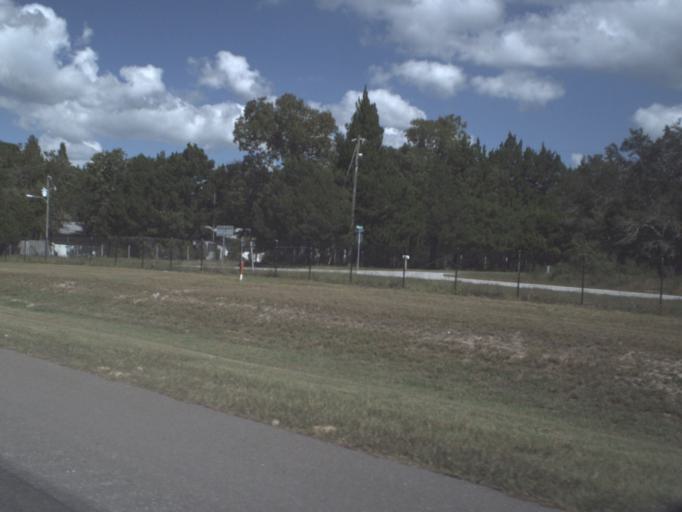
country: US
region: Florida
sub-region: Hernando County
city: Brookridge
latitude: 28.4998
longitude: -82.4768
